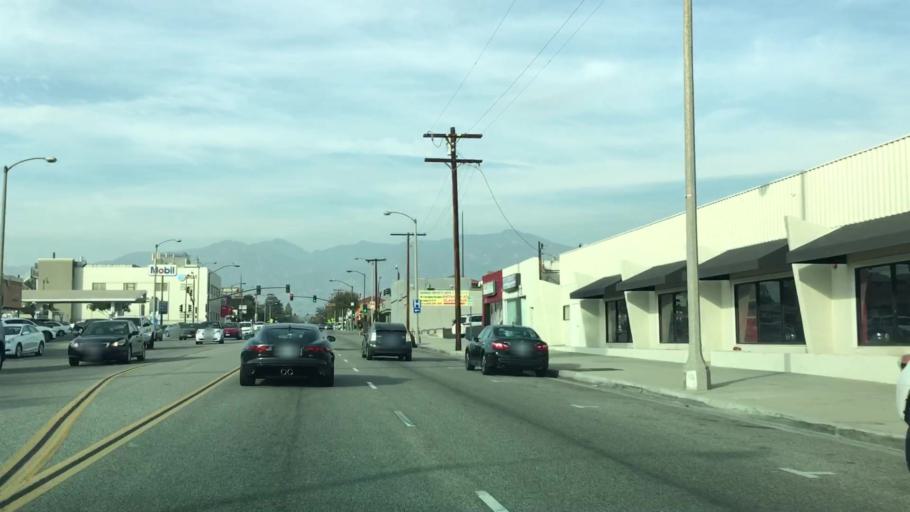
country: US
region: California
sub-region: Los Angeles County
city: East San Gabriel
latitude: 34.1019
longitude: -118.0909
